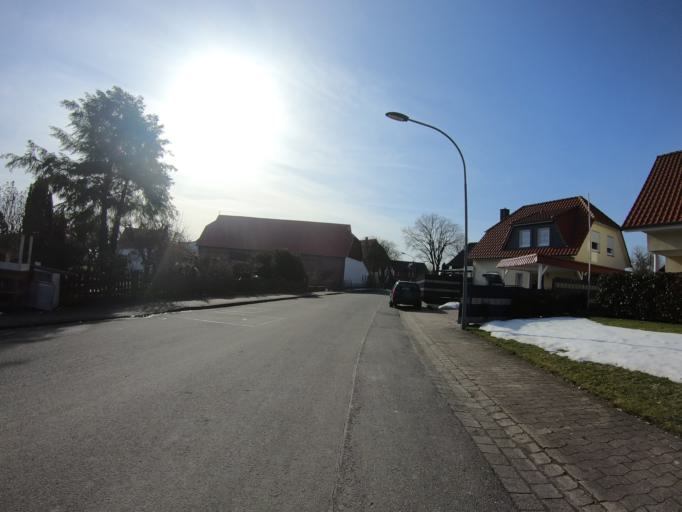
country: DE
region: Lower Saxony
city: Wasbuttel
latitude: 52.4099
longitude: 10.5642
